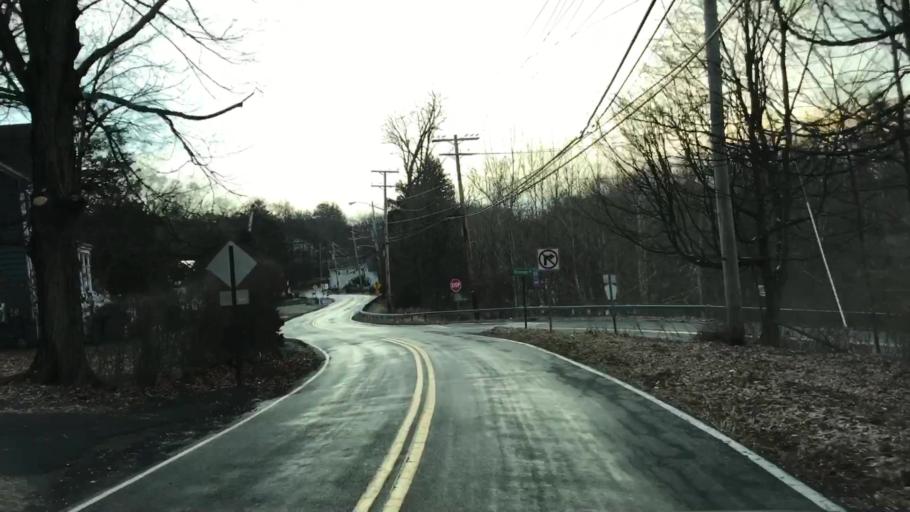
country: US
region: New York
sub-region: Rockland County
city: Stony Point
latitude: 41.2332
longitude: -74.0015
